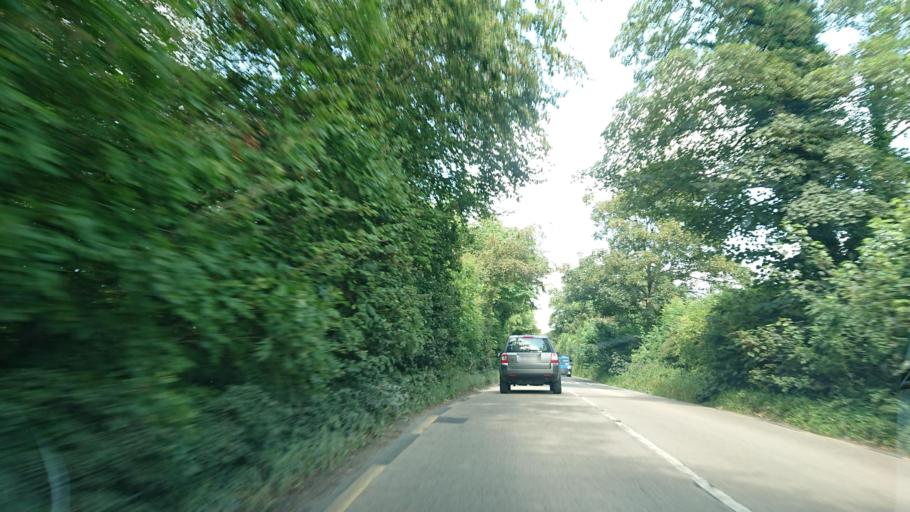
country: IE
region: Leinster
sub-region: Kildare
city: Sallins
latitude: 53.2707
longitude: -6.6725
